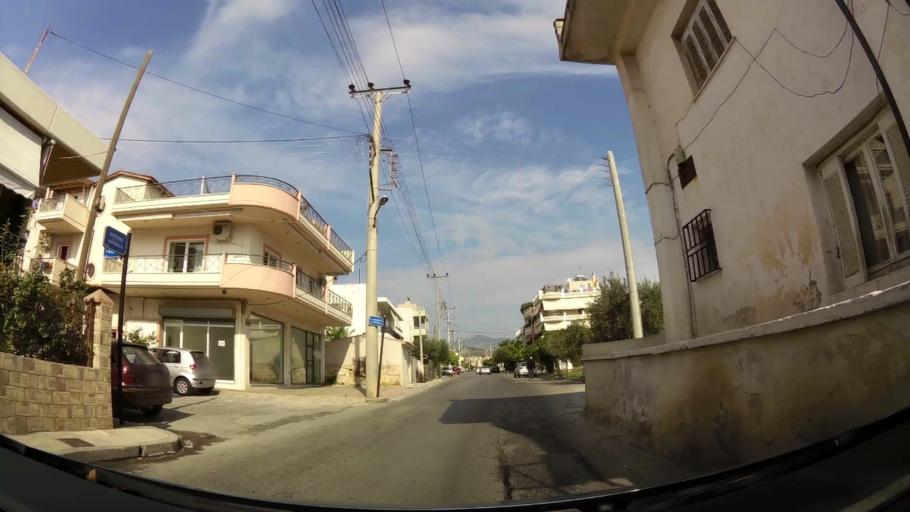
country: GR
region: Attica
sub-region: Nomarchia Athinas
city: Kamateron
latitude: 38.0436
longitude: 23.7092
